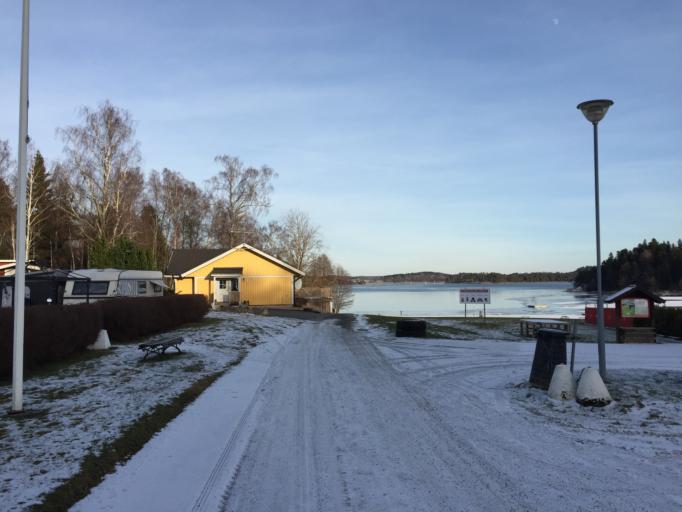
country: SE
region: Stockholm
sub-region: Sodertalje Kommun
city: Pershagen
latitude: 59.0975
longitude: 17.6505
